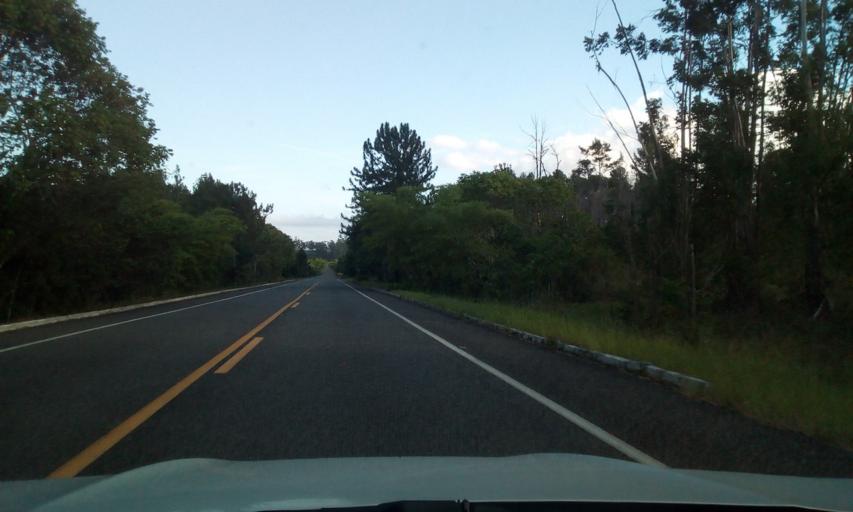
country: BR
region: Bahia
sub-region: Entre Rios
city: Entre Rios
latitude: -12.3169
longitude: -37.9044
